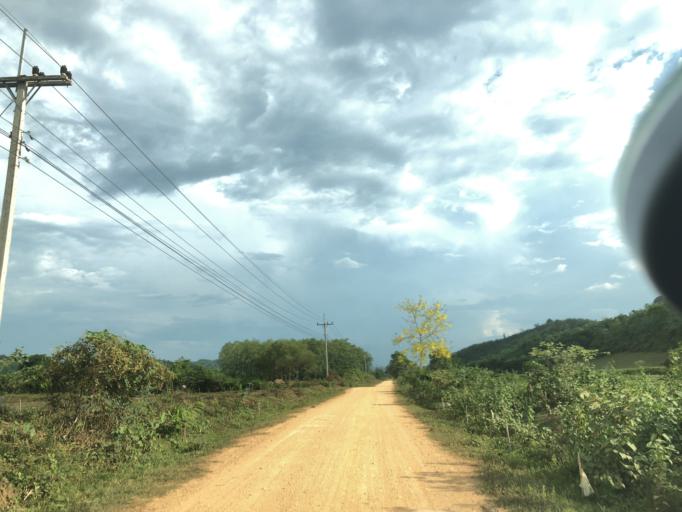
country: TH
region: Loei
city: Chiang Khan
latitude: 18.0049
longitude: 101.4205
